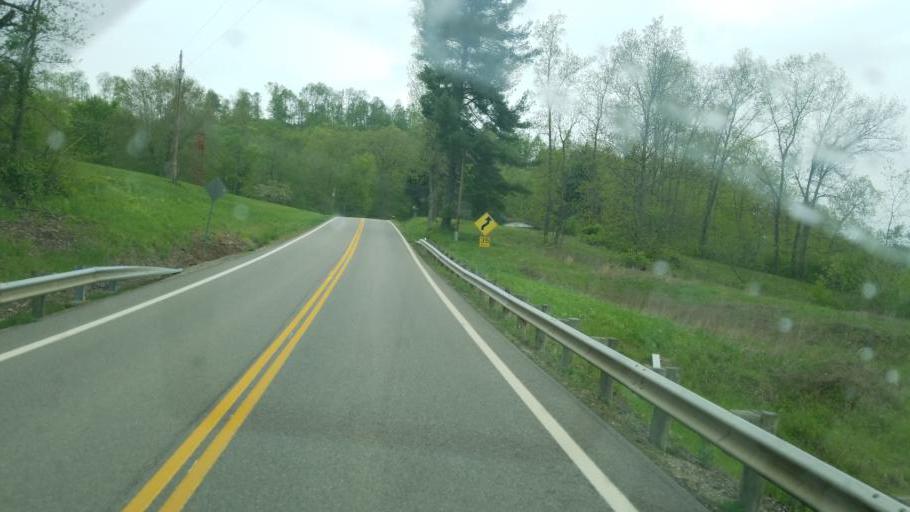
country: US
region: Ohio
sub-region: Guernsey County
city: Mantua
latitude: 40.1532
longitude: -81.6023
